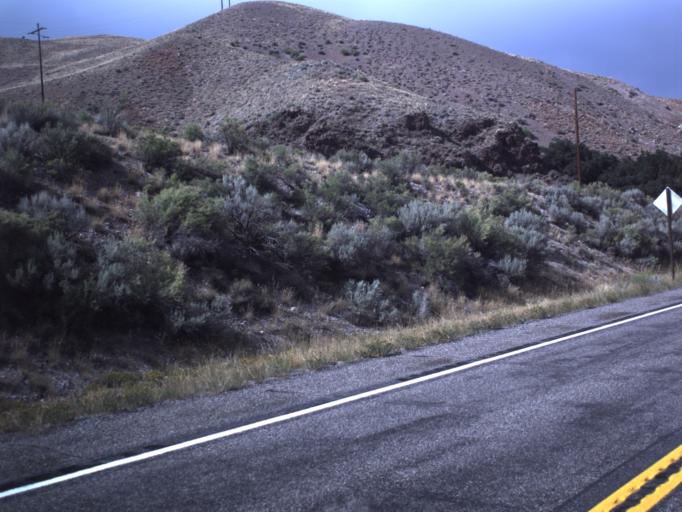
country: US
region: Utah
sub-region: Sevier County
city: Monroe
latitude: 38.4848
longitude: -112.2442
